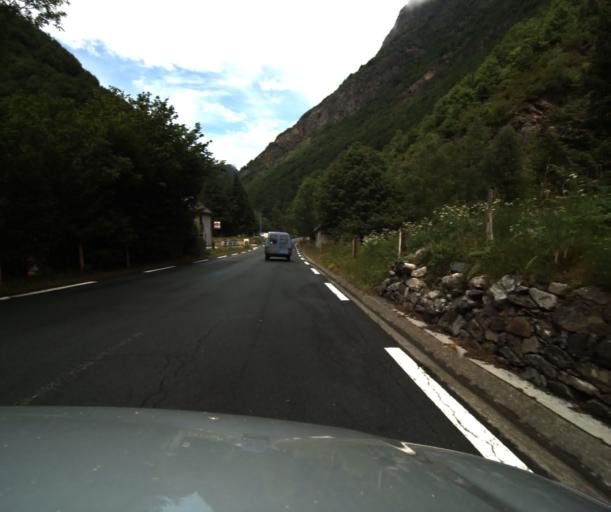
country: FR
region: Midi-Pyrenees
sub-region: Departement des Hautes-Pyrenees
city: Luz-Saint-Sauveur
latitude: 42.8010
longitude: 0.0135
